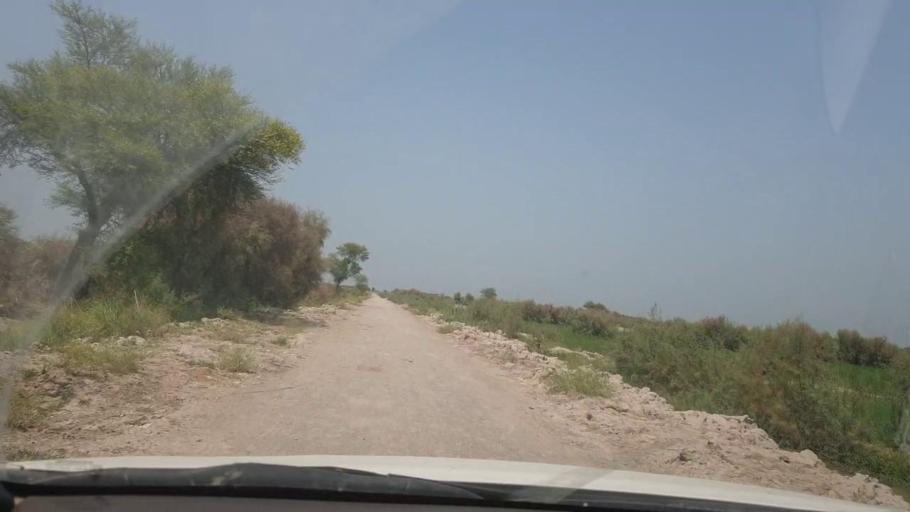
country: PK
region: Sindh
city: Lakhi
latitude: 27.8860
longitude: 68.7430
